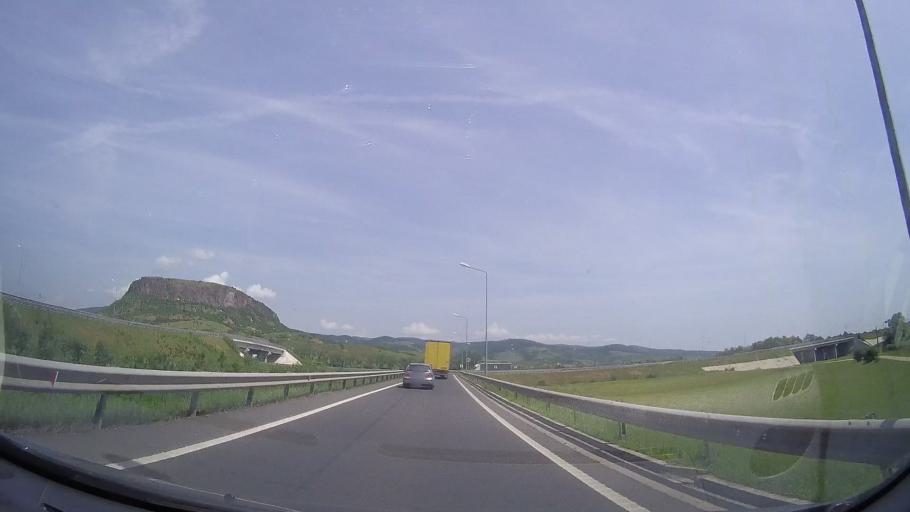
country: RO
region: Hunedoara
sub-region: Comuna Rapoltu Mare
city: Rapoltu Mare
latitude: 45.8479
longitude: 23.0452
